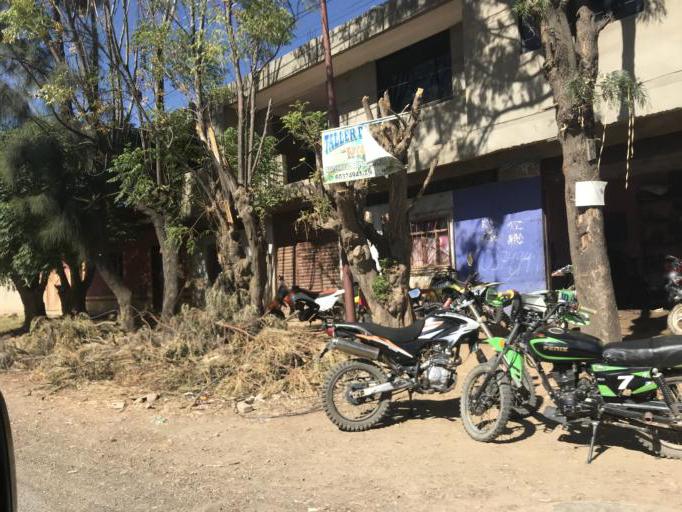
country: BO
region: Cochabamba
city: Cliza
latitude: -17.5850
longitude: -65.9178
